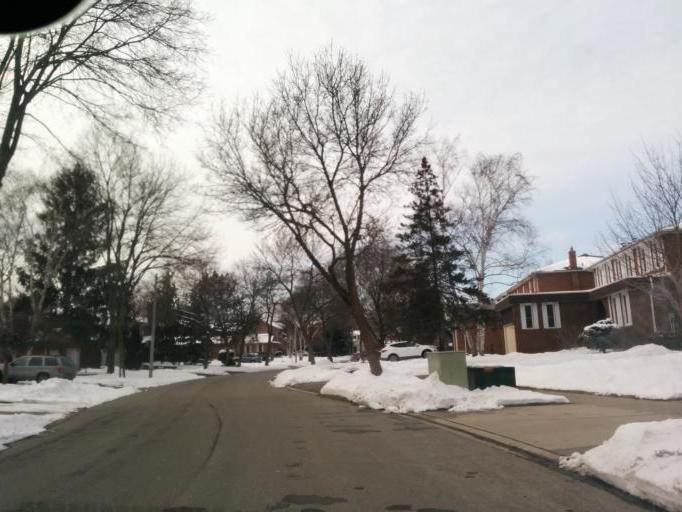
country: CA
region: Ontario
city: Mississauga
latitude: 43.5376
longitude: -79.6596
